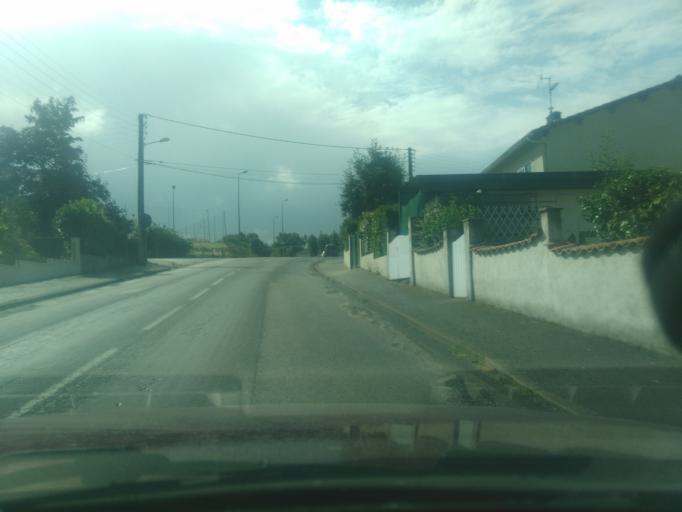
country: FR
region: Poitou-Charentes
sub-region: Departement des Deux-Sevres
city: Parthenay
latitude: 46.6365
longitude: -0.2628
